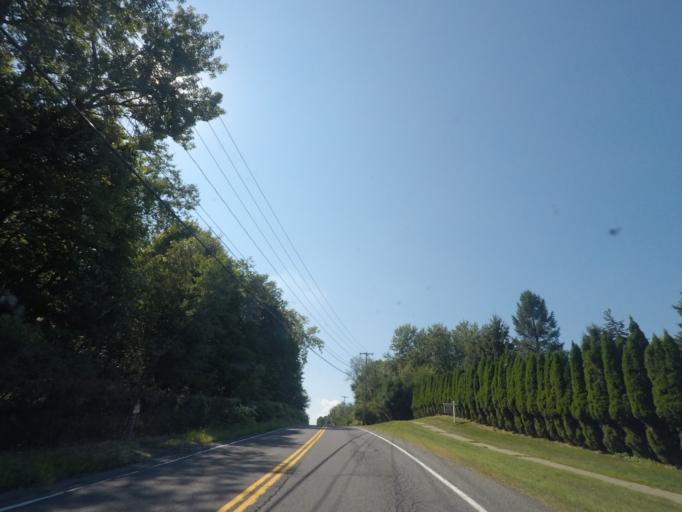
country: US
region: New York
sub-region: Albany County
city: Menands
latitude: 42.7146
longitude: -73.7351
